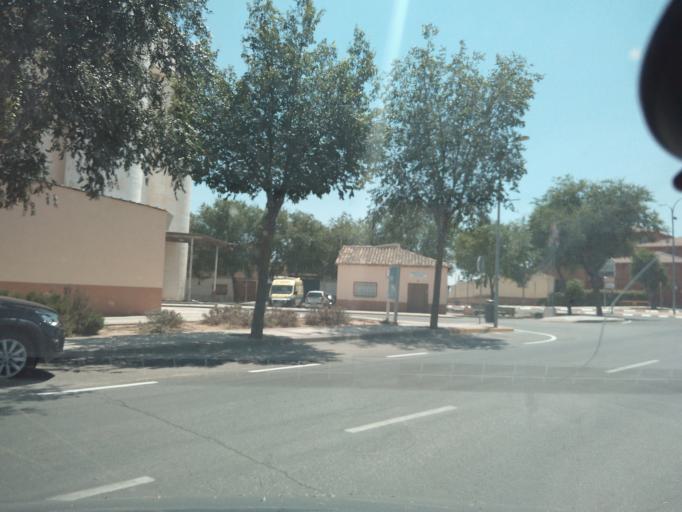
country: ES
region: Castille-La Mancha
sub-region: Province of Toledo
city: Villacanas
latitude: 39.6162
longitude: -3.3396
